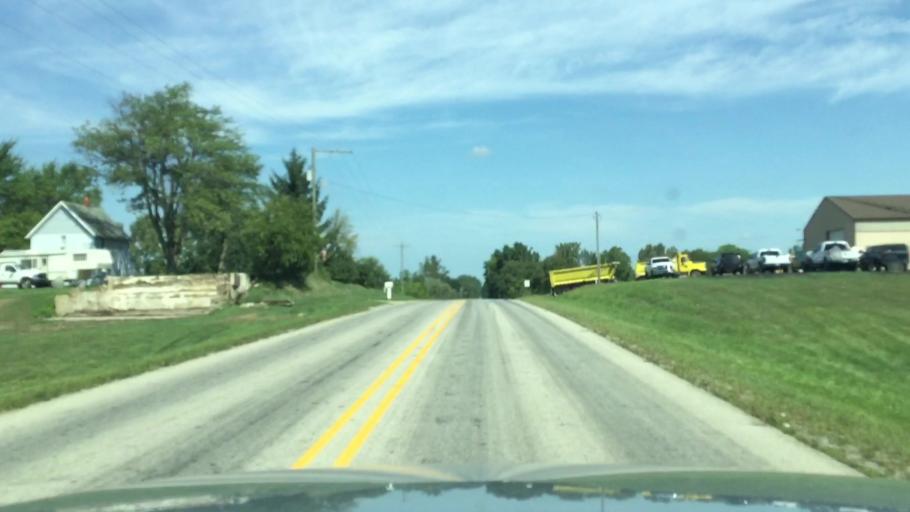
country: US
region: Michigan
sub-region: Lenawee County
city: Manitou Beach-Devils Lake
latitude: 42.0161
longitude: -84.2762
